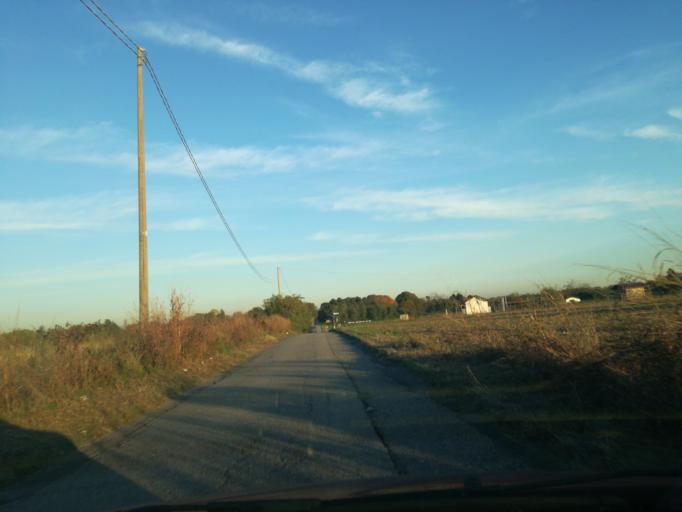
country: IT
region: Lombardy
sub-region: Provincia di Monza e Brianza
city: Burago di Molgora
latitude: 45.6060
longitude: 9.3847
